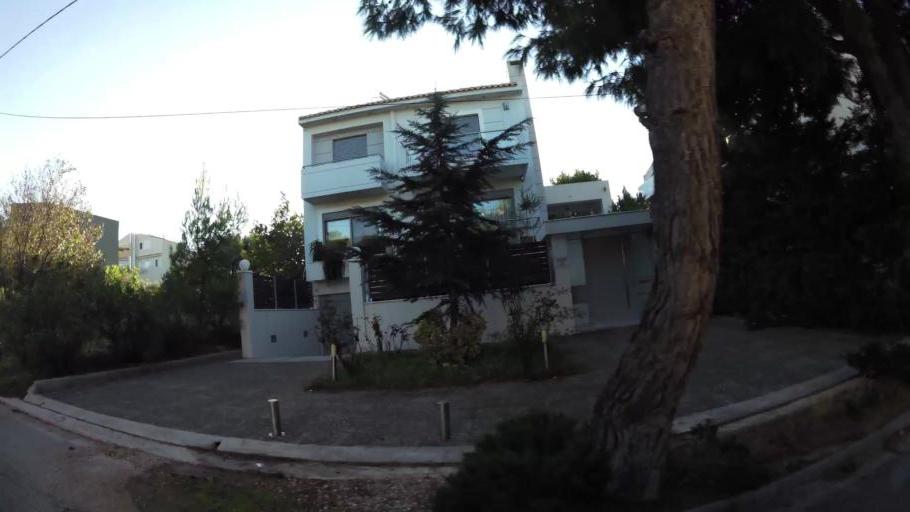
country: GR
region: Attica
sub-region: Nomarchia Anatolikis Attikis
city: Gerakas
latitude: 38.0337
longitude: 23.8500
